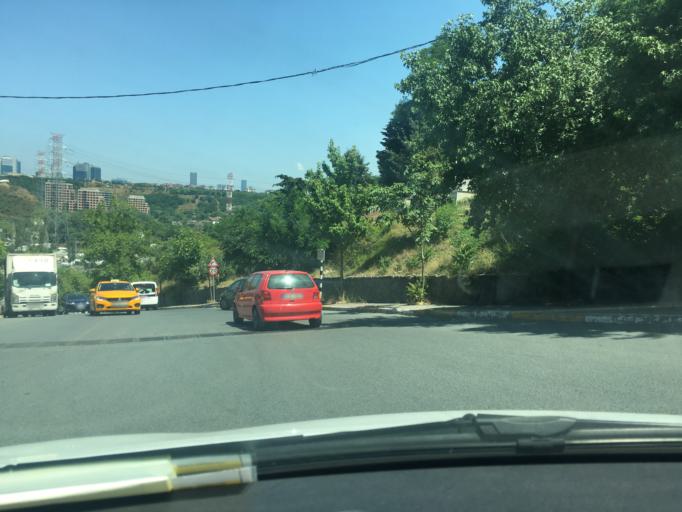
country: TR
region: Istanbul
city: Sisli
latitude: 41.0839
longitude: 28.9460
